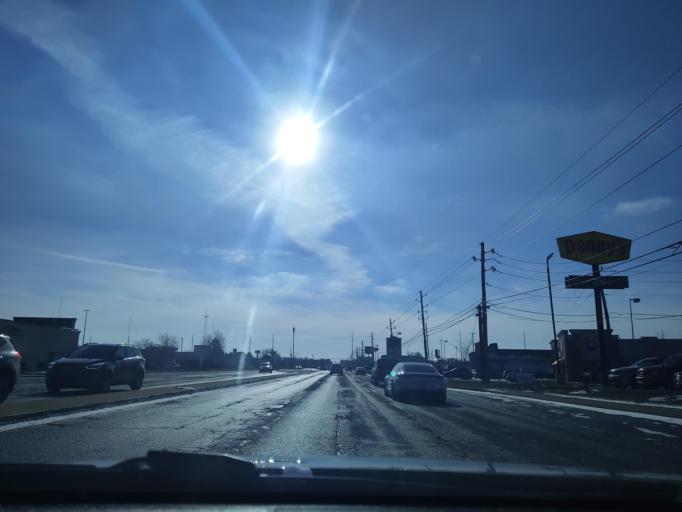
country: US
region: Indiana
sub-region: Boone County
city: Zionsville
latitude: 39.9152
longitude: -86.2244
